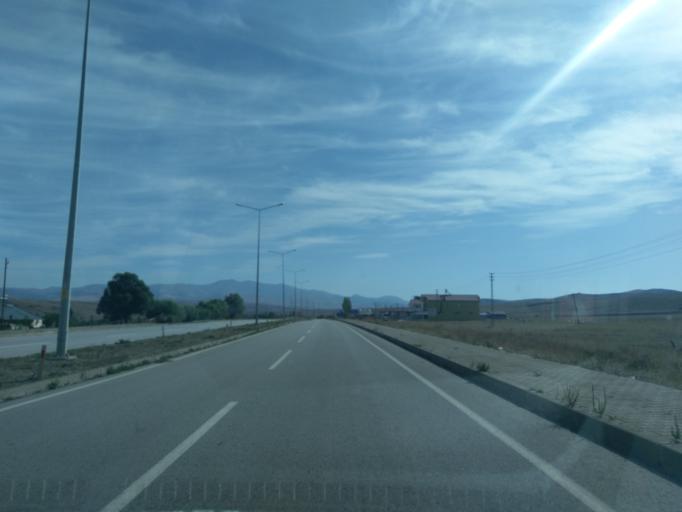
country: TR
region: Sivas
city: Imranli
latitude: 39.8710
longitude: 38.1308
